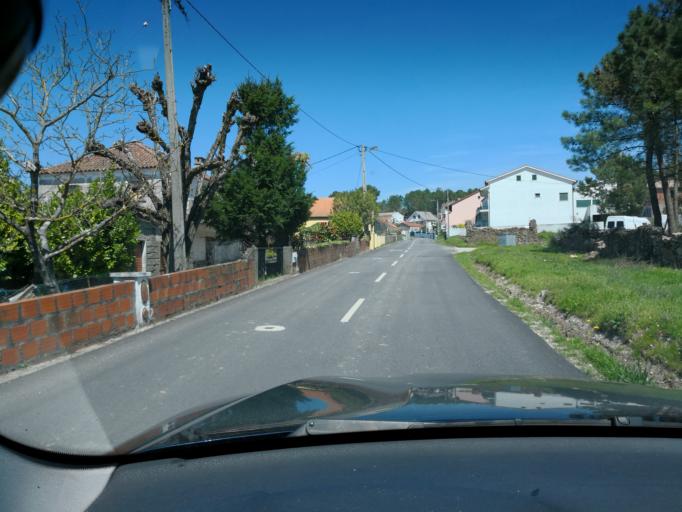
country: PT
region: Vila Real
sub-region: Vila Real
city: Vila Real
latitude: 41.3109
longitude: -7.6955
